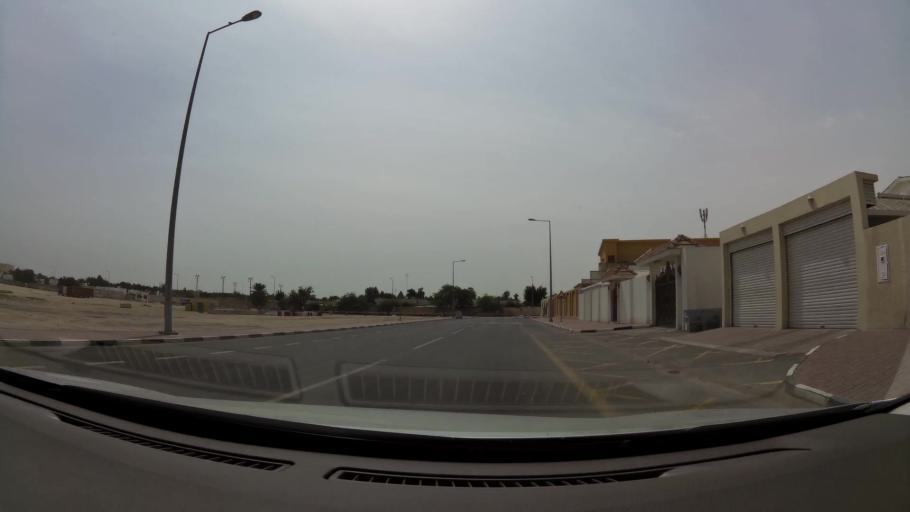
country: QA
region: Baladiyat ad Dawhah
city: Doha
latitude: 25.2657
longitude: 51.4870
